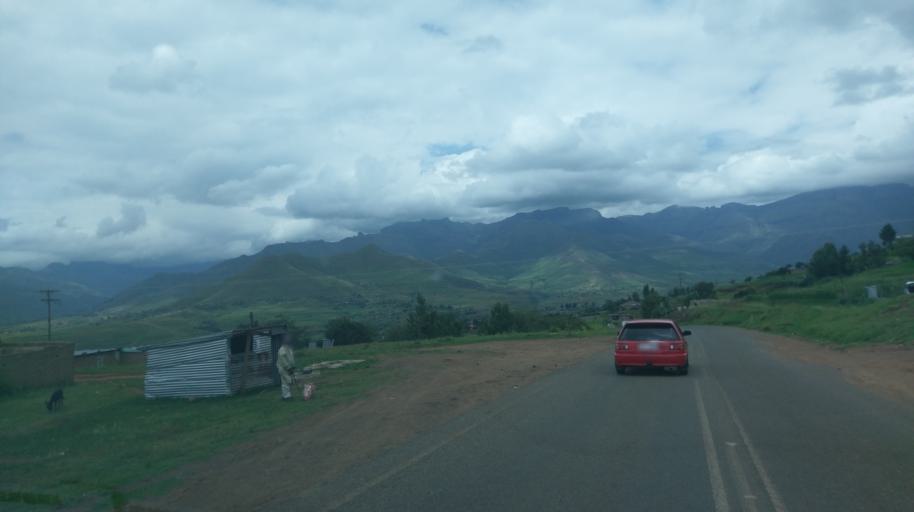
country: LS
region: Leribe
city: Leribe
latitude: -29.0277
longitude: 28.2321
